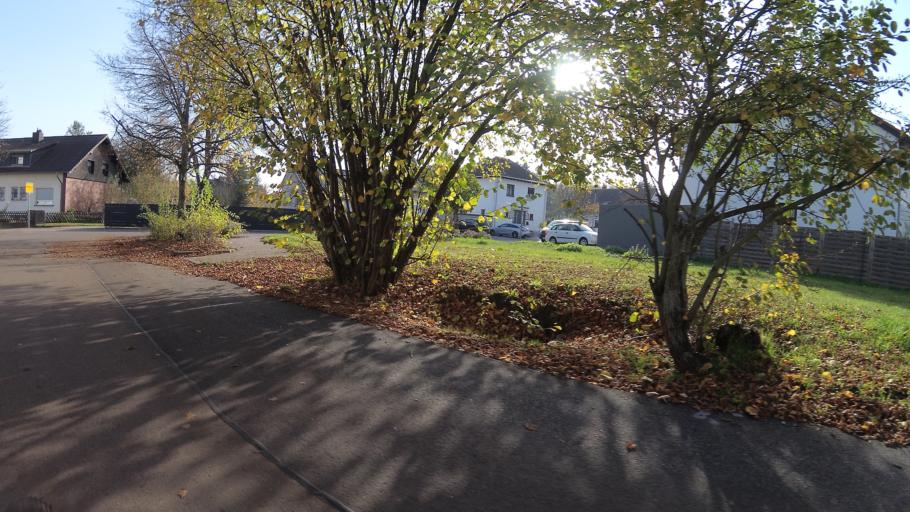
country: DE
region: Saarland
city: Bexbach
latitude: 49.3533
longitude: 7.2720
